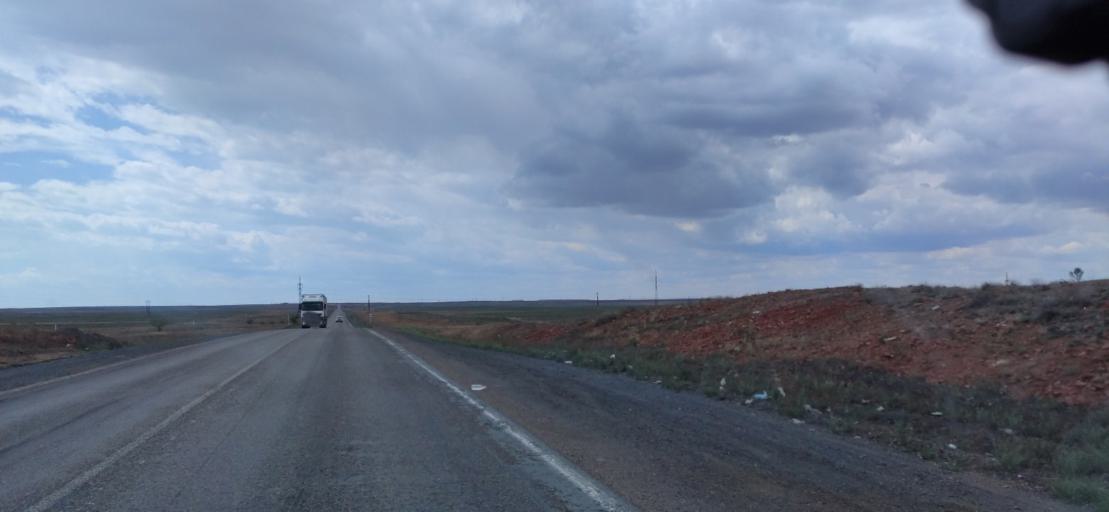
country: KZ
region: Qaraghandy
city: Saryshaghan
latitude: 46.0678
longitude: 73.6009
